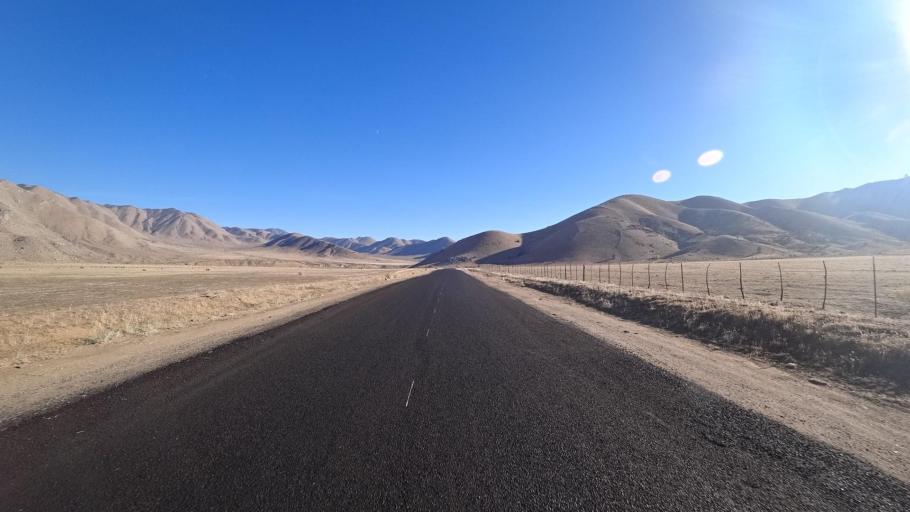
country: US
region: California
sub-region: Kern County
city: Weldon
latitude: 35.6249
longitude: -118.2603
